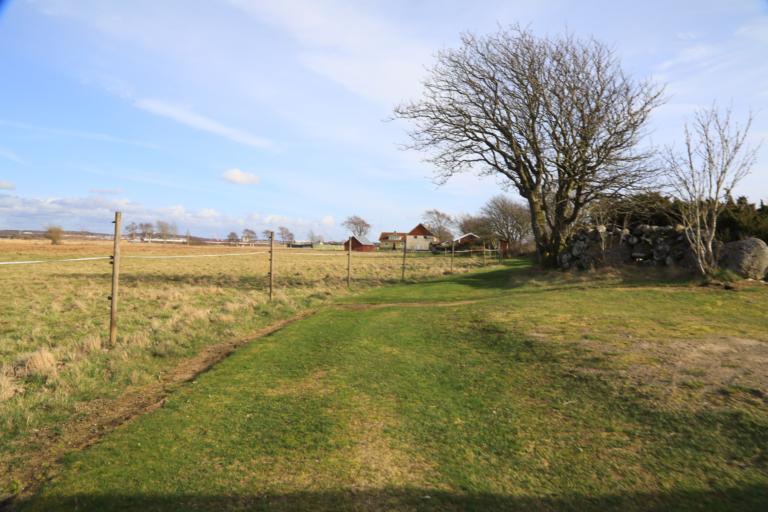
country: SE
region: Halland
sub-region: Varbergs Kommun
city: Varberg
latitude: 57.1252
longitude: 12.2186
